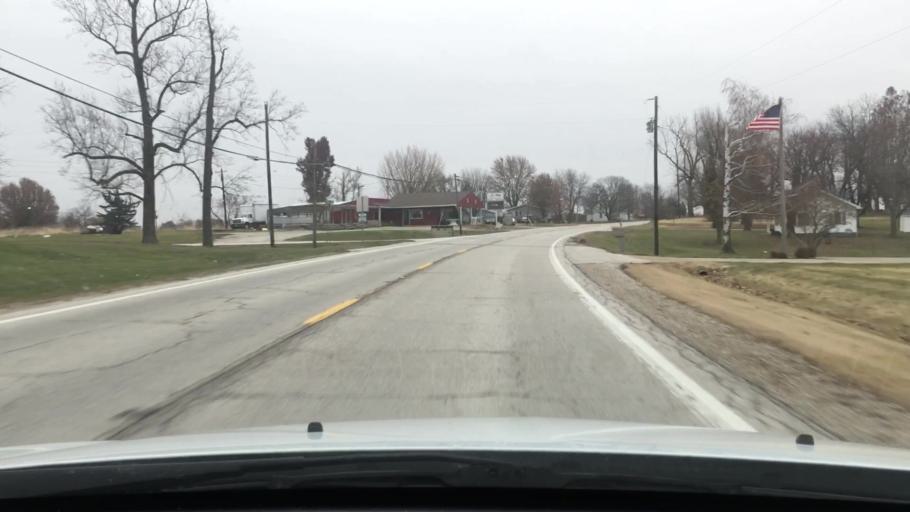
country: US
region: Illinois
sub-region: Pike County
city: Pittsfield
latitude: 39.5754
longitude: -90.9107
